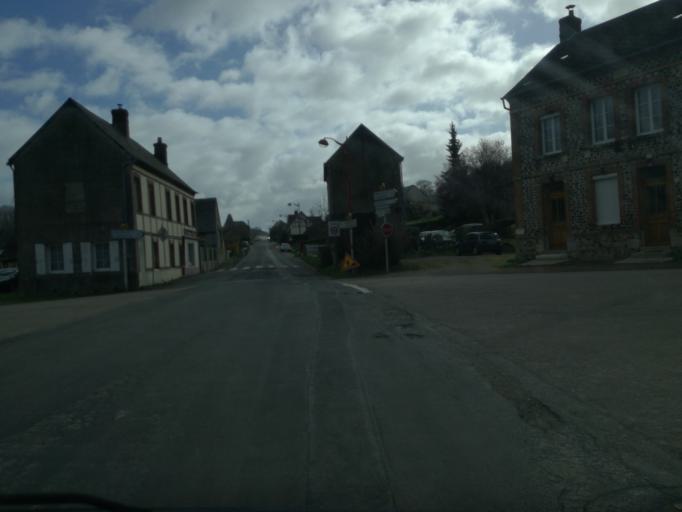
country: FR
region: Haute-Normandie
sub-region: Departement de la Seine-Maritime
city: Bretteville-du-Grand-Caux
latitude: 49.7042
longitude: 0.4439
